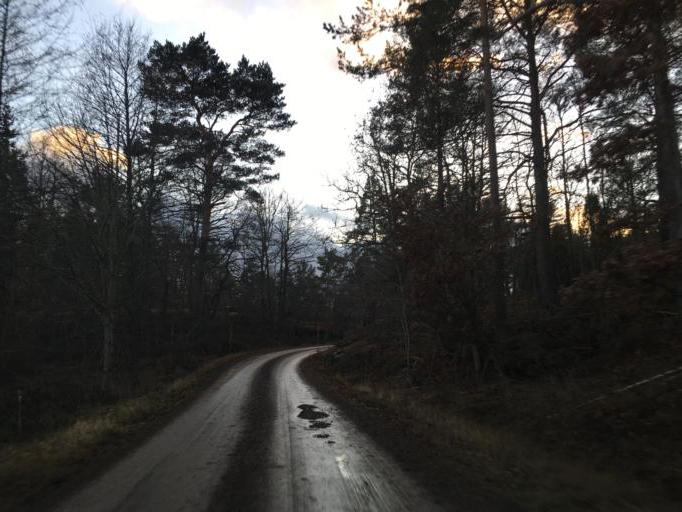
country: SE
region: Kalmar
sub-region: Vasterviks Kommun
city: Vaestervik
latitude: 57.6028
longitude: 16.5304
